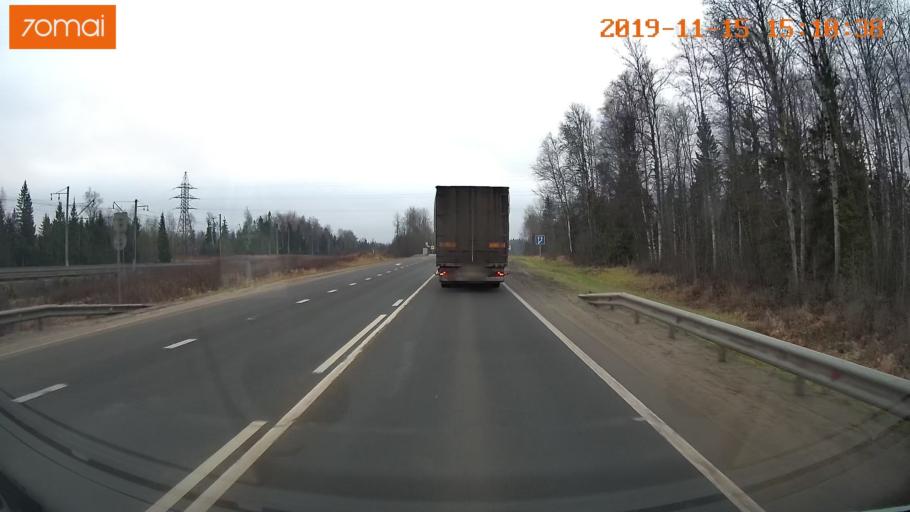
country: RU
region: Jaroslavl
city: Prechistoye
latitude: 58.3458
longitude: 40.2522
